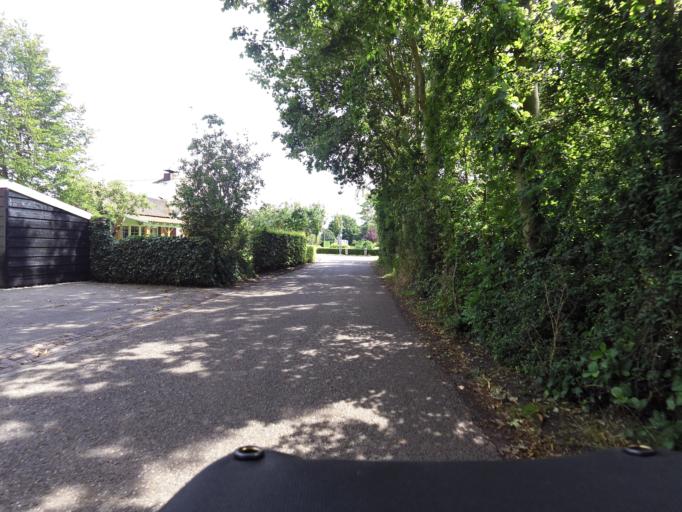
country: NL
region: South Holland
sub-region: Gemeente Goeree-Overflakkee
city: Ouddorp
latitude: 51.8067
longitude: 3.9258
